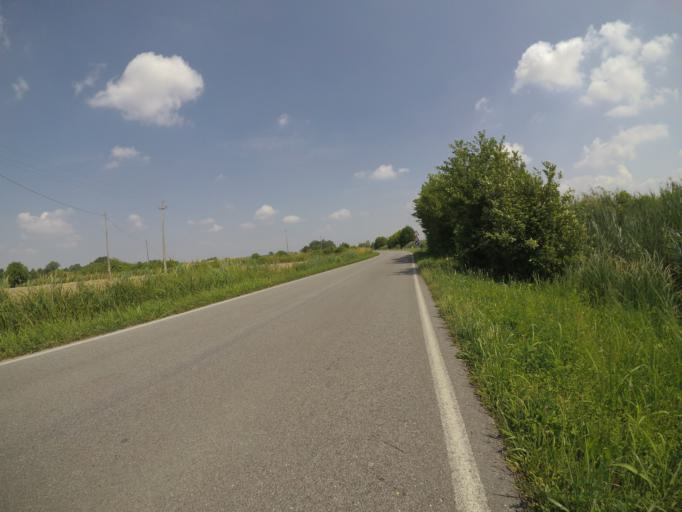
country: IT
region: Friuli Venezia Giulia
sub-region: Provincia di Udine
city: Teor
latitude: 45.8746
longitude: 13.0878
